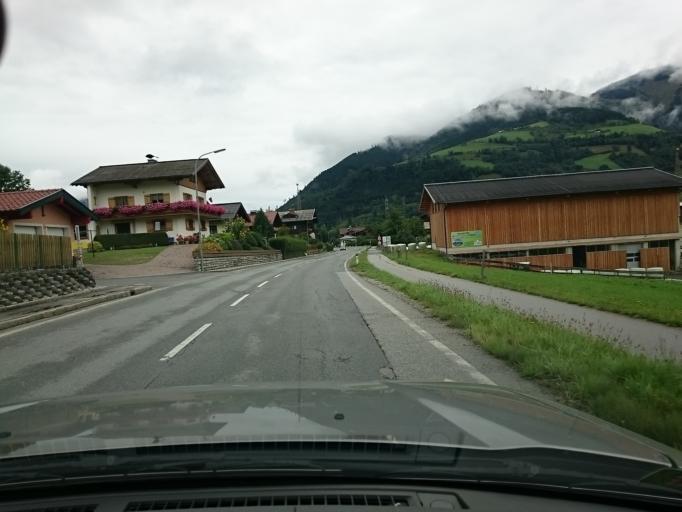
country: AT
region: Salzburg
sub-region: Politischer Bezirk Zell am See
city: Bruck an der Grossglocknerstrasse
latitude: 47.2764
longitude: 12.8263
